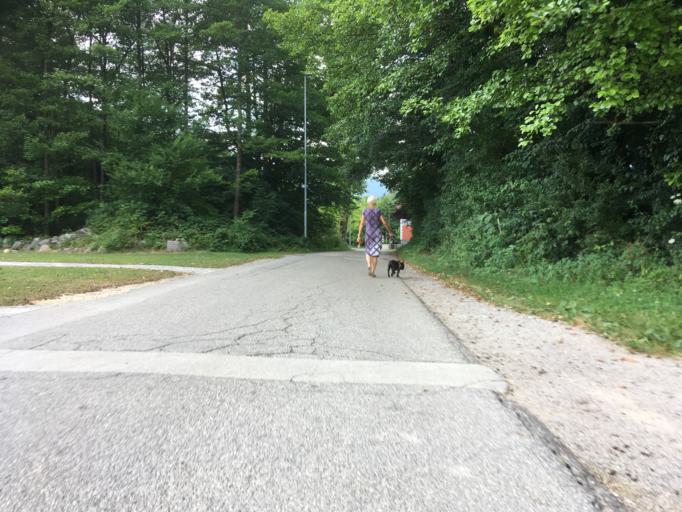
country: SI
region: Kocevje
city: Kocevje
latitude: 45.6408
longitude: 14.8505
